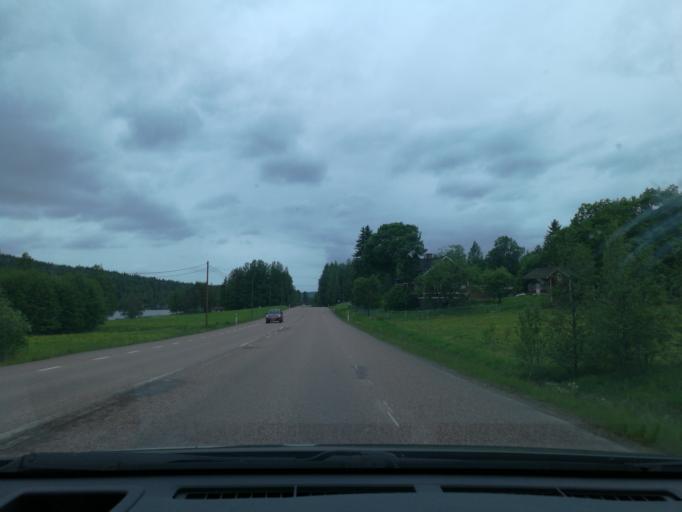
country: SE
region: Dalarna
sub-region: Ludvika Kommun
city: Ludvika
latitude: 60.1484
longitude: 15.2753
